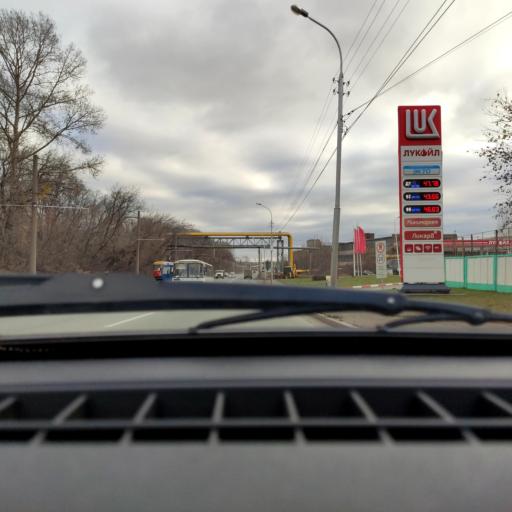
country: RU
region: Bashkortostan
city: Ufa
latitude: 54.7983
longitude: 56.1189
